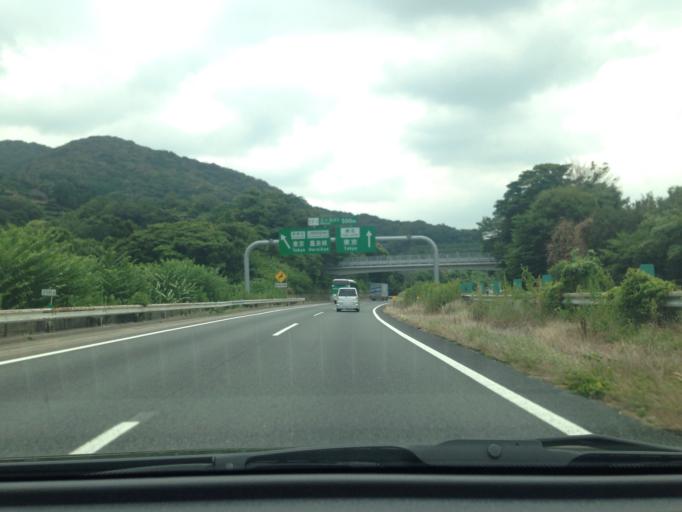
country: JP
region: Aichi
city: Shinshiro
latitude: 34.8327
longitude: 137.5371
